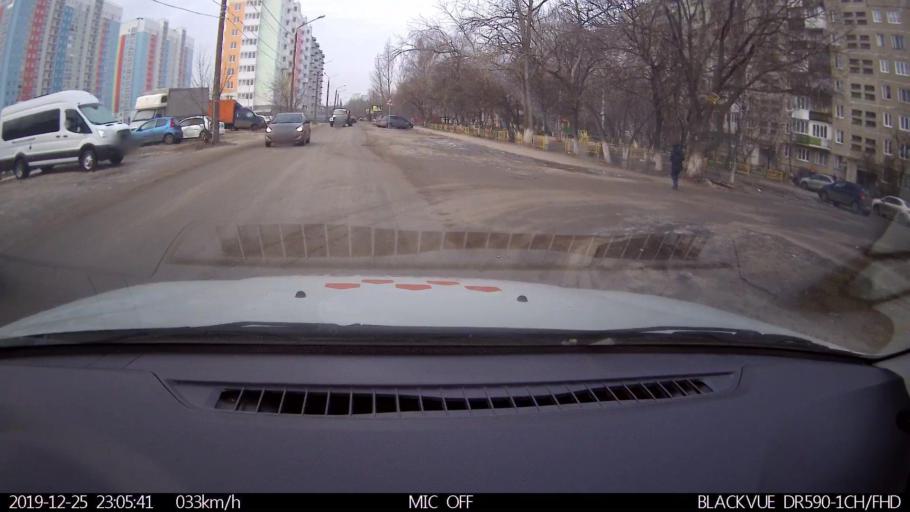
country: RU
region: Nizjnij Novgorod
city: Gorbatovka
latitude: 56.3609
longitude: 43.8062
